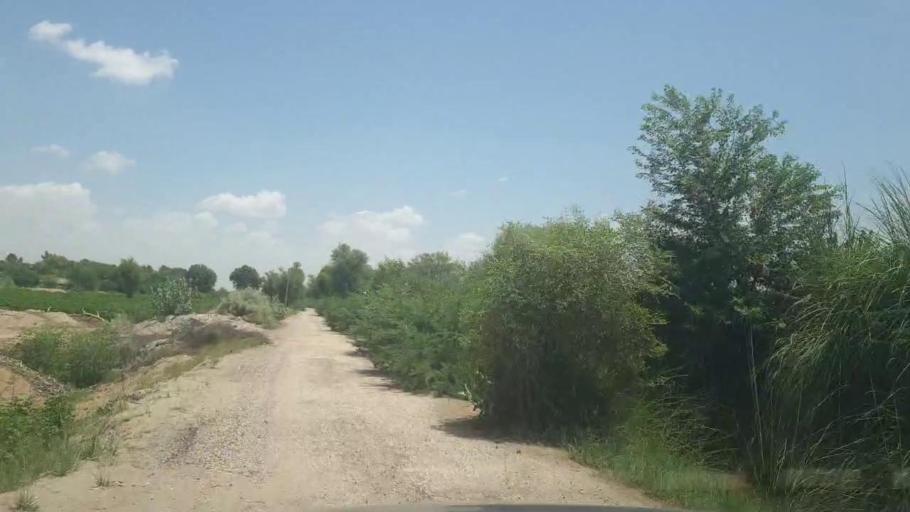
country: PK
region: Sindh
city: Kot Diji
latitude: 27.2630
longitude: 69.0241
